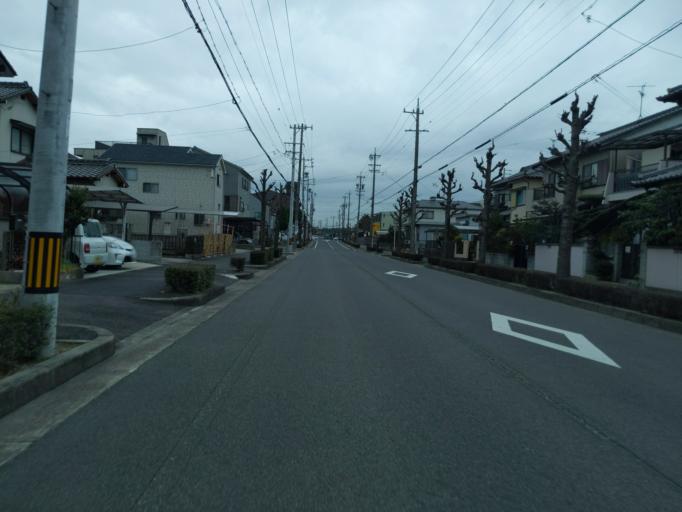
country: JP
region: Aichi
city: Kasugai
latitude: 35.2534
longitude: 136.9515
